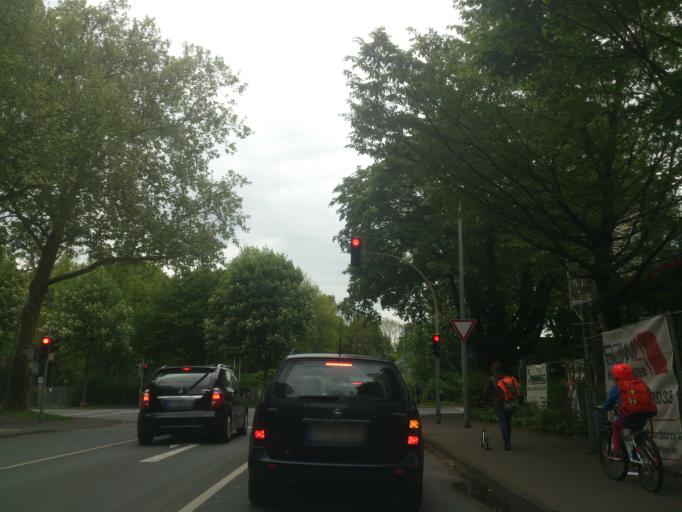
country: DE
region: North Rhine-Westphalia
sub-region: Regierungsbezirk Detmold
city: Paderborn
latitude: 51.7292
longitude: 8.7436
